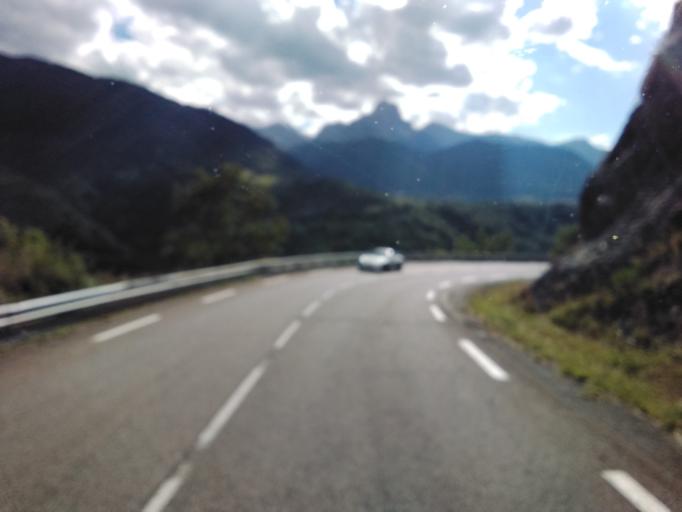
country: FR
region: Provence-Alpes-Cote d'Azur
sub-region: Departement des Hautes-Alpes
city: Saint-Bonnet-en-Champsaur
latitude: 44.8057
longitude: 5.9556
